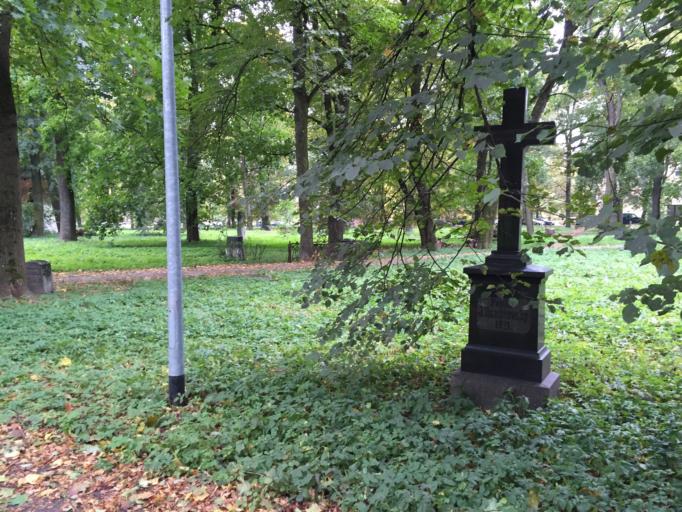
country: LV
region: Riga
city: Riga
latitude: 56.9737
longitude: 24.1455
